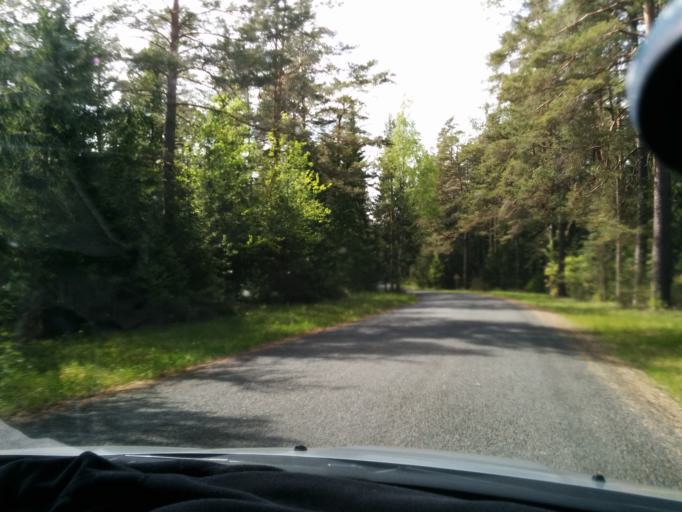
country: EE
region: Harju
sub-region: Loksa linn
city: Loksa
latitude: 59.5777
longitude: 25.6079
